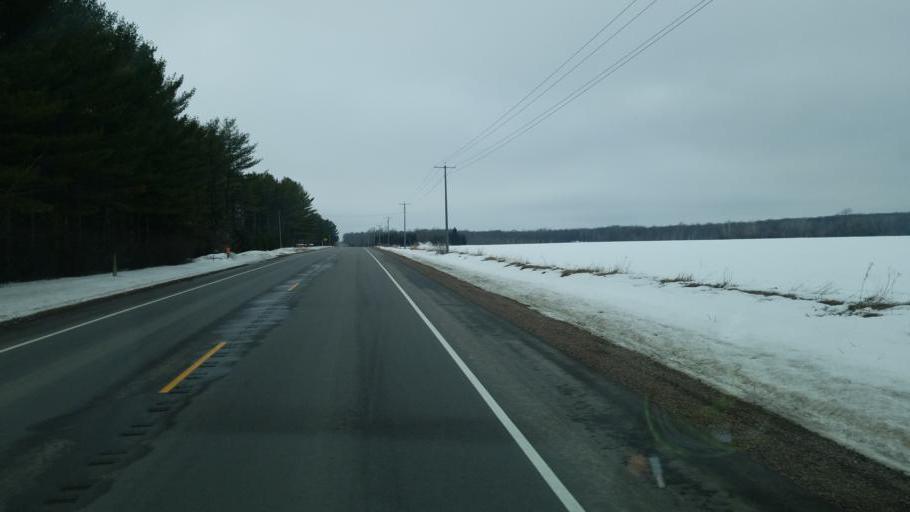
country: US
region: Wisconsin
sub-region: Wood County
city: Marshfield
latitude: 44.6563
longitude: -90.2441
